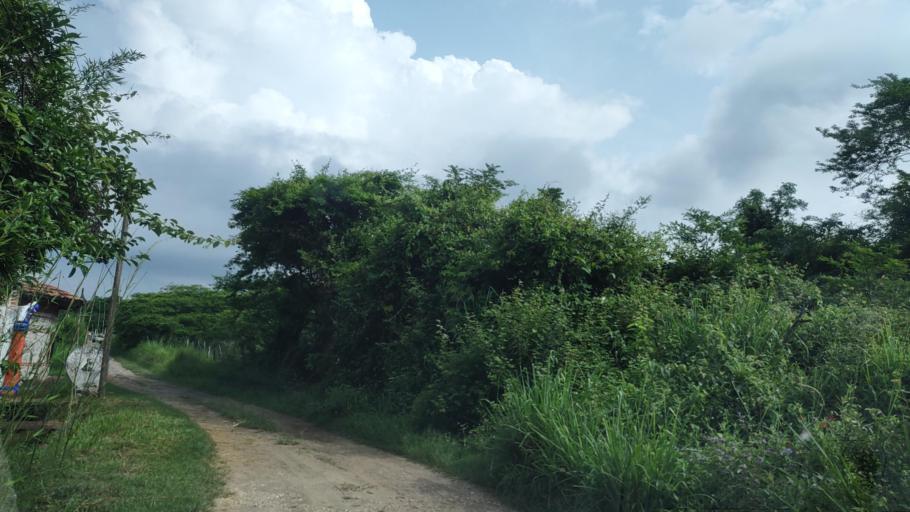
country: MX
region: Veracruz
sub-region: Coatepec
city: Bella Esperanza
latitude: 19.4477
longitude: -96.8268
